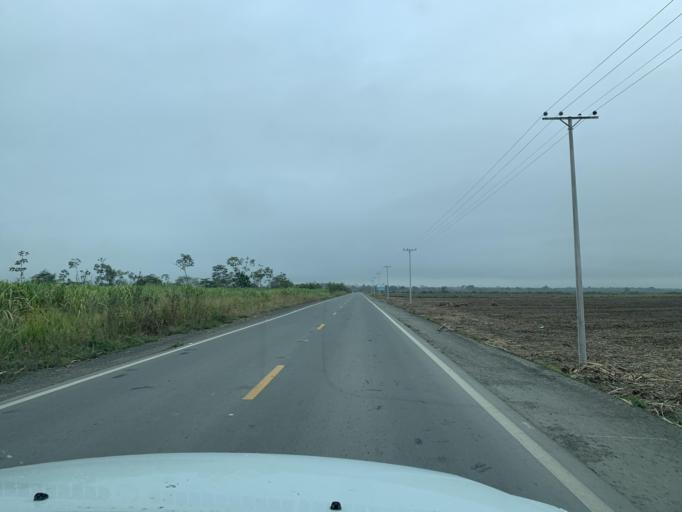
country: EC
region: Guayas
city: Coronel Marcelino Mariduena
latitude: -2.3064
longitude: -79.5051
